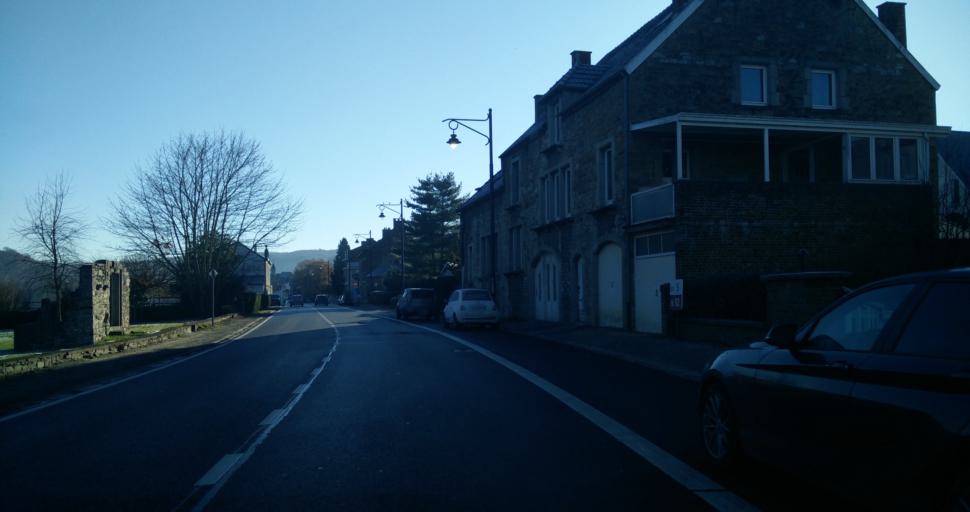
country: BE
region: Wallonia
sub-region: Province de Namur
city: Namur
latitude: 50.4262
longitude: 4.8698
